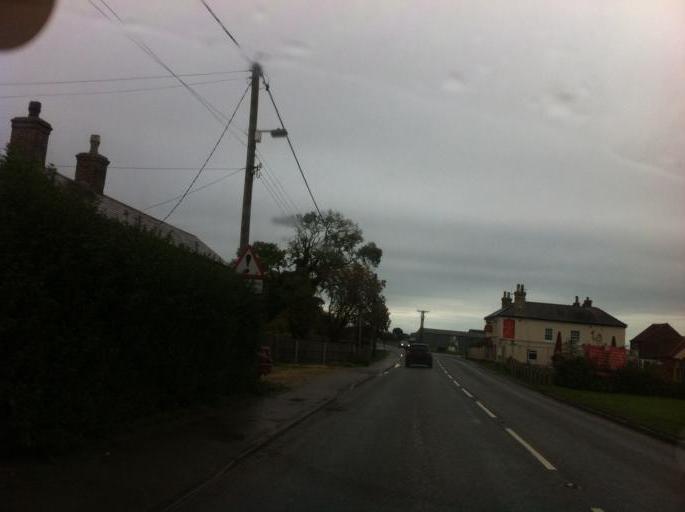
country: GB
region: England
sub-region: Lincolnshire
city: Spilsby
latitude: 53.0317
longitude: 0.1125
